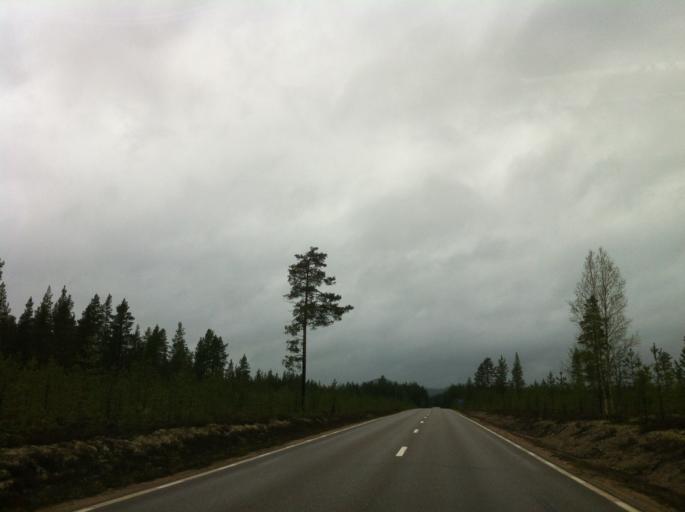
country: SE
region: Jaemtland
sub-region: Harjedalens Kommun
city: Sveg
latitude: 62.1401
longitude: 13.9859
